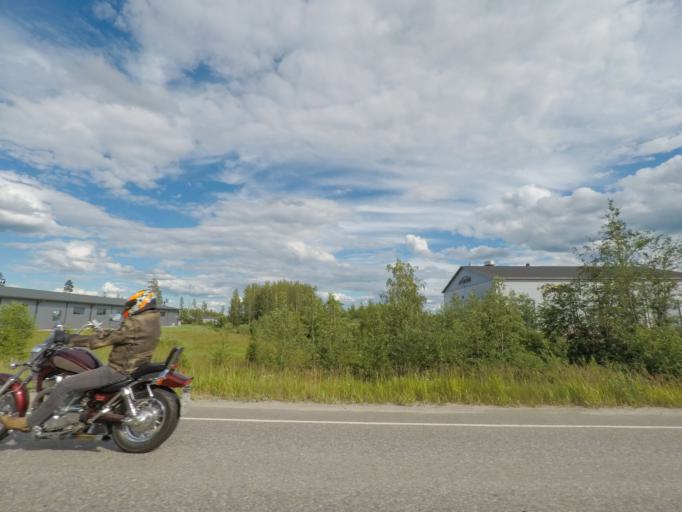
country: FI
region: Paijanne Tavastia
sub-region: Lahti
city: Lahti
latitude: 60.9343
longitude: 25.5890
